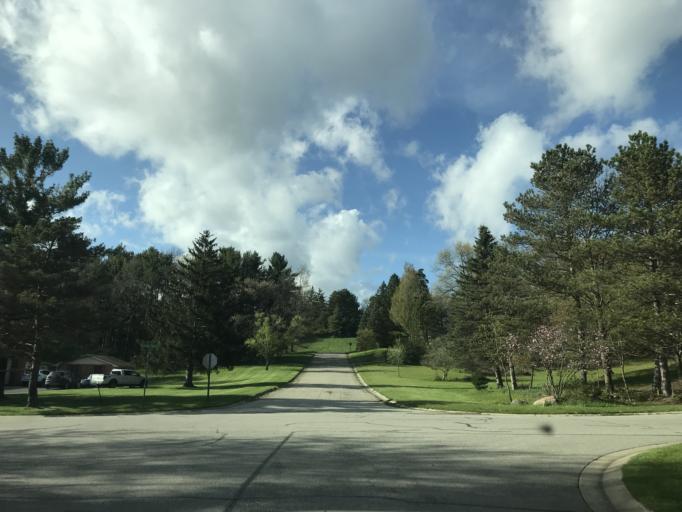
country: US
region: Michigan
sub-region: Livingston County
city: Brighton
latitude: 42.5306
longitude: -83.7163
